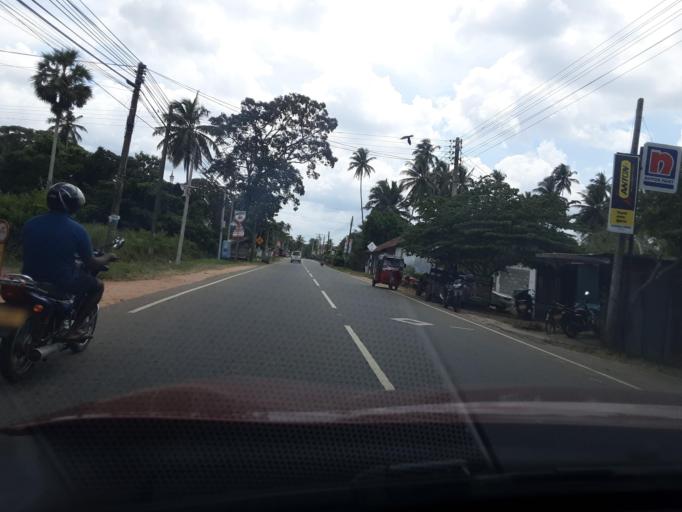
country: LK
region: North Western
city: Kuliyapitiya
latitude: 7.4512
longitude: 80.1705
